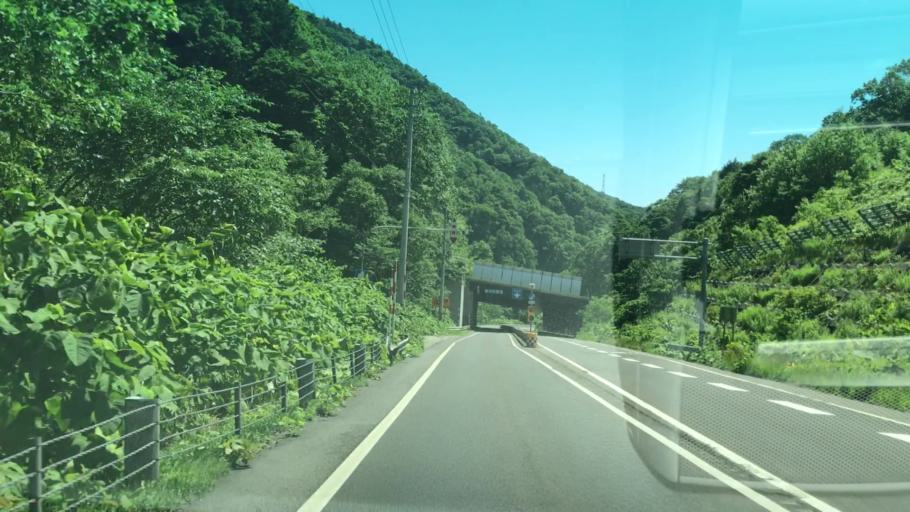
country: JP
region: Hokkaido
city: Yoichi
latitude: 43.0471
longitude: 140.6810
